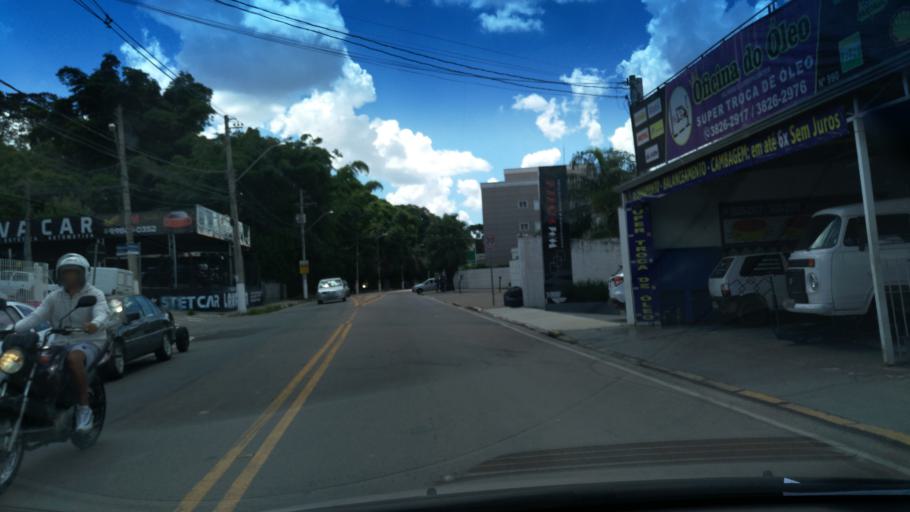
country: BR
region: Sao Paulo
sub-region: Vinhedo
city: Vinhedo
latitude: -23.0185
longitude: -46.9825
